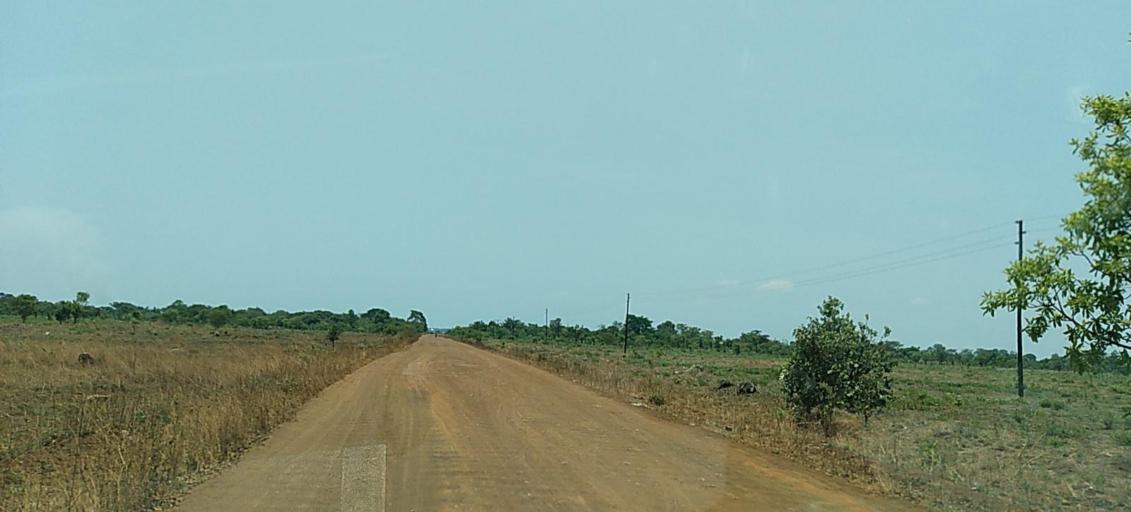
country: ZM
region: Copperbelt
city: Mpongwe
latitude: -13.6801
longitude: 27.8579
